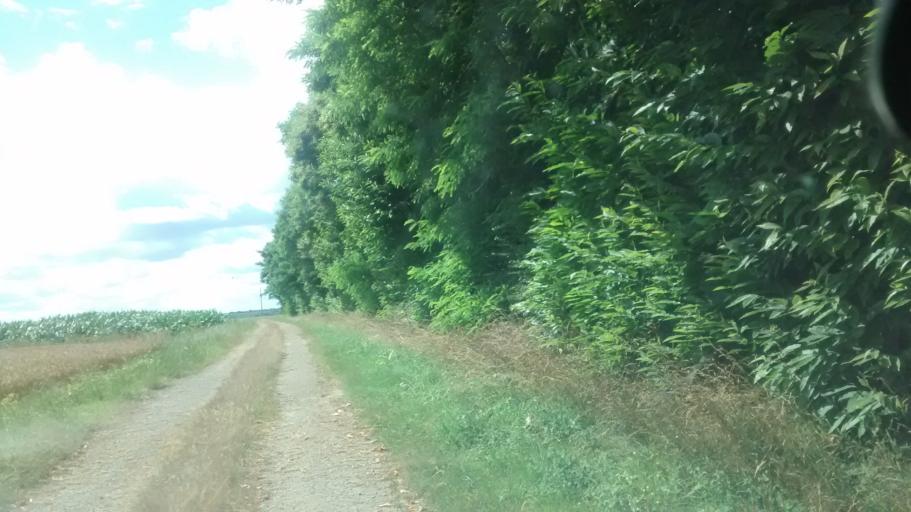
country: FR
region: Brittany
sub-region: Departement d'Ille-et-Vilaine
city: Grand-Fougeray
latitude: 47.7722
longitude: -1.7539
